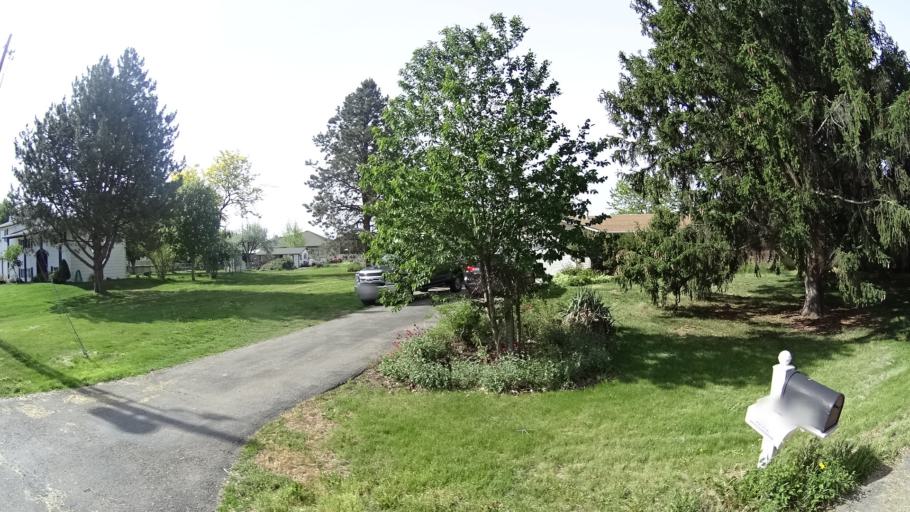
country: US
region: Idaho
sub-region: Ada County
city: Garden City
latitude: 43.5654
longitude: -116.2977
